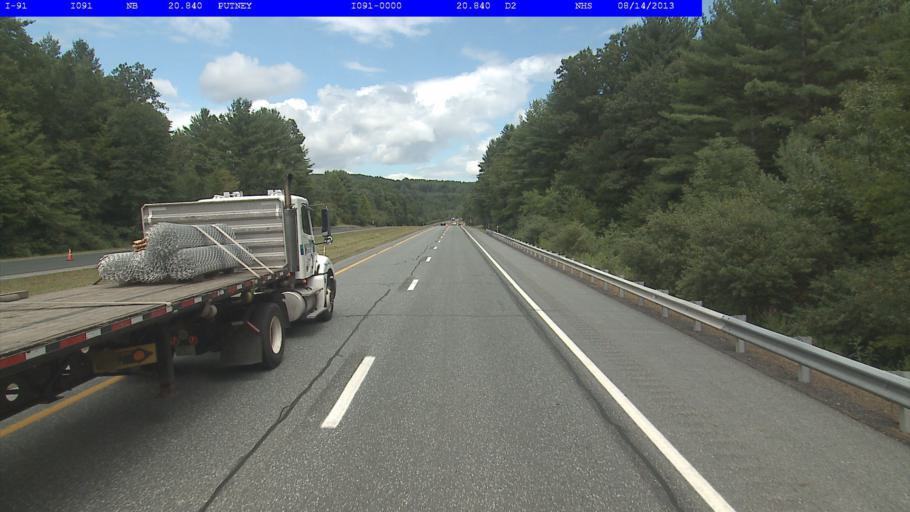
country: US
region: New Hampshire
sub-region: Cheshire County
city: Westmoreland
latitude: 42.9842
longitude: -72.4804
